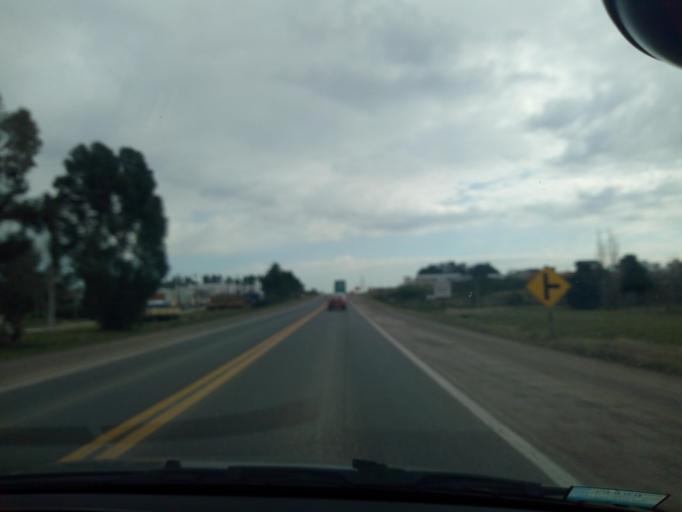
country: AR
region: Buenos Aires
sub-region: Partido de Tandil
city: Tandil
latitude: -37.3252
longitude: -59.0965
